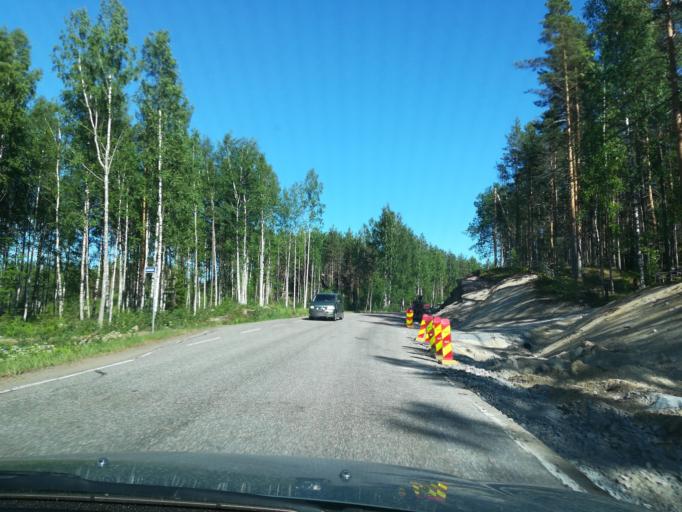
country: FI
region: Southern Savonia
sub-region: Mikkeli
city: Puumala
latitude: 61.4674
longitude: 28.3238
